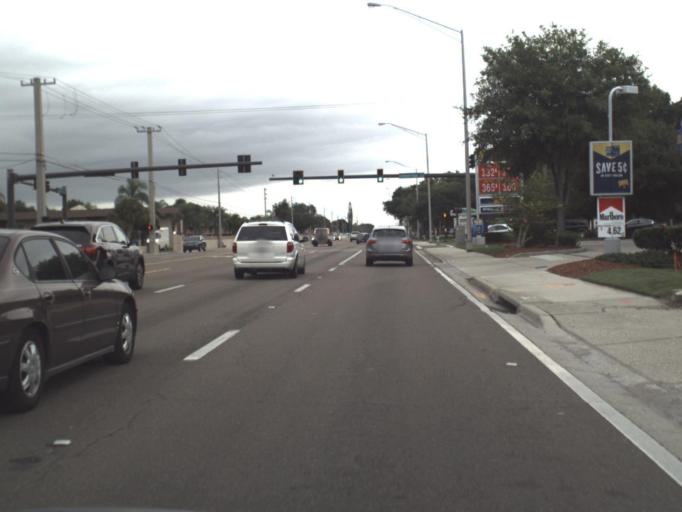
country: US
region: Florida
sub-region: Sarasota County
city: Southgate
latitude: 27.2987
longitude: -82.5068
